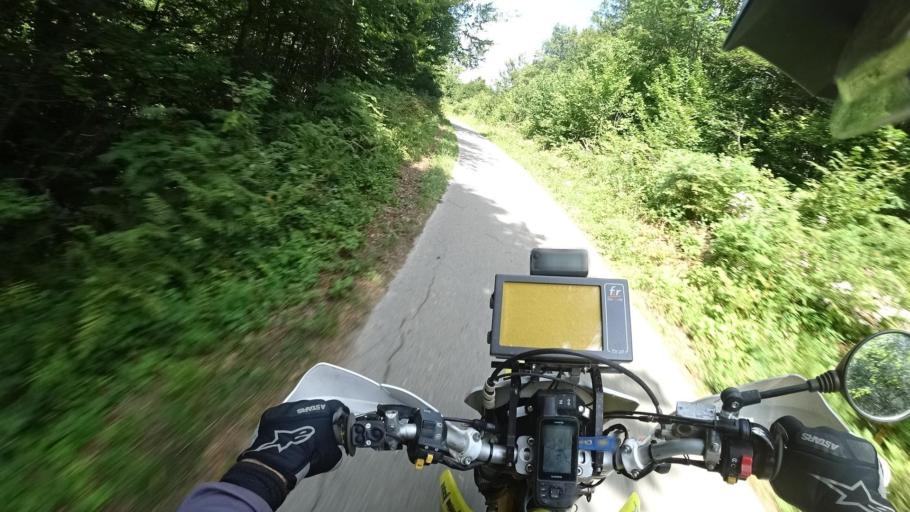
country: HR
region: Licko-Senjska
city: Brinje
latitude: 45.1031
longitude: 15.1154
